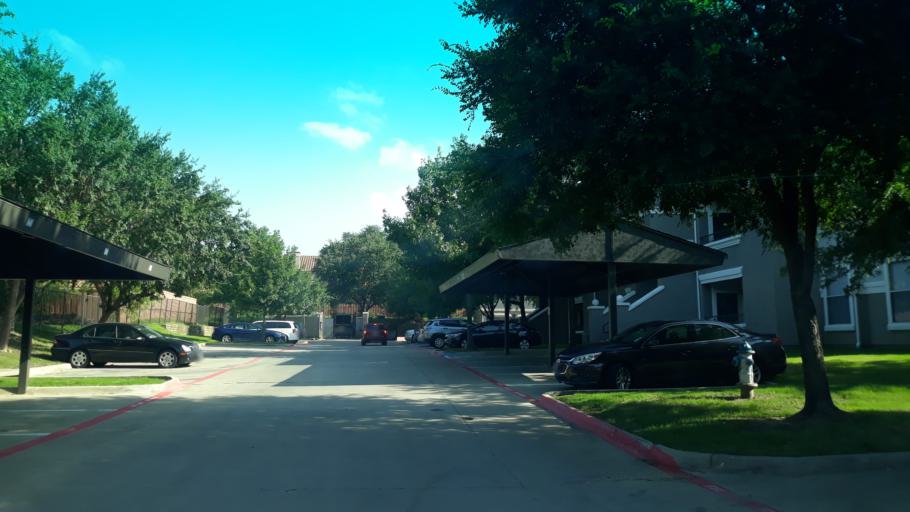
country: US
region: Texas
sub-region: Dallas County
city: Irving
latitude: 32.8619
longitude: -96.9829
